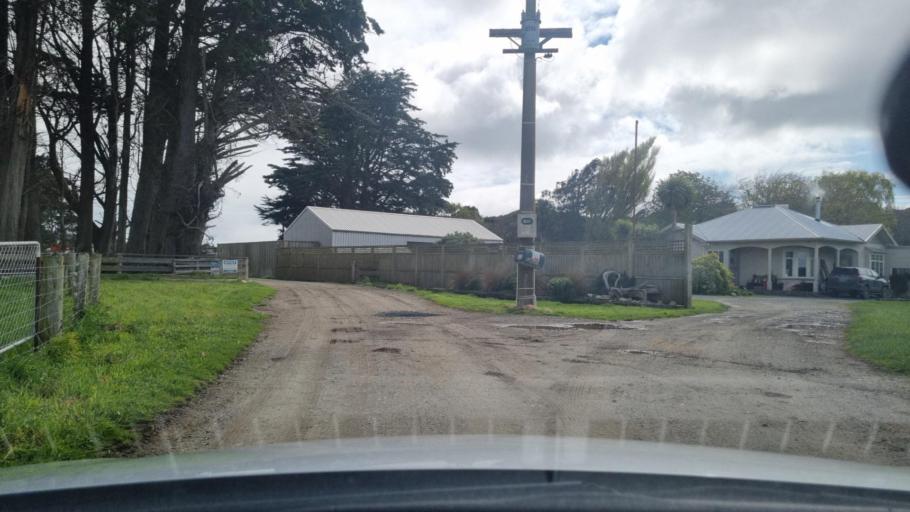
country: NZ
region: Southland
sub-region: Invercargill City
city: Bluff
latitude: -46.5251
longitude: 168.2978
